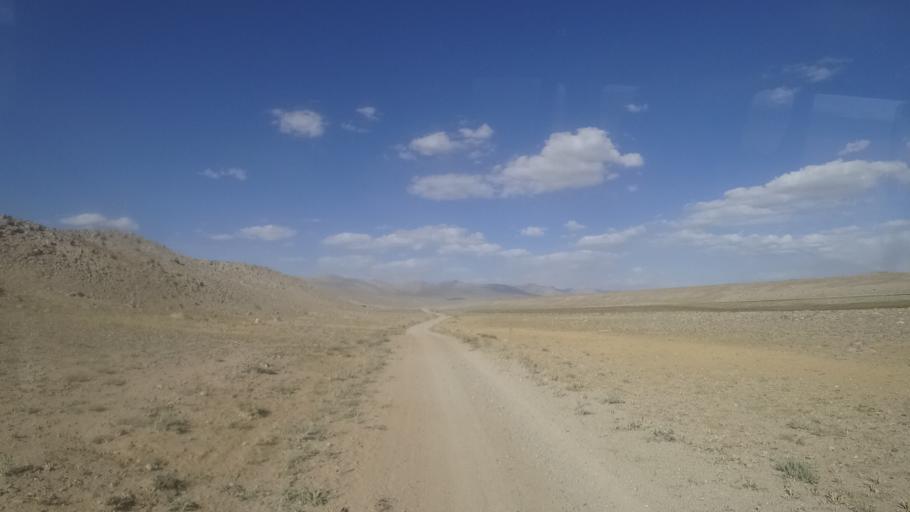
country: AF
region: Badakhshan
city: Khandud
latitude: 37.4259
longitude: 73.2410
